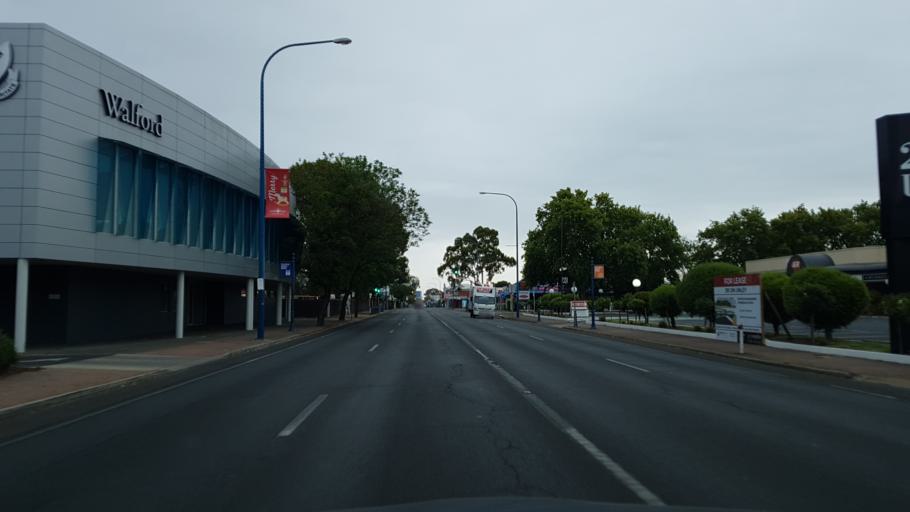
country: AU
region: South Australia
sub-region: Unley
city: Unley Park
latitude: -34.9596
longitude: 138.6082
